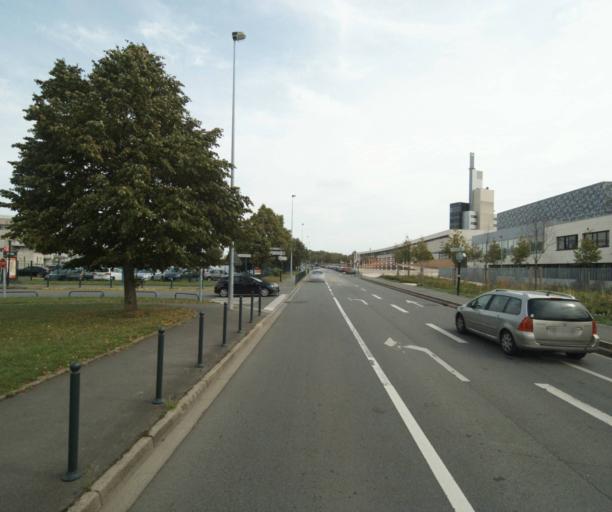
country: FR
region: Nord-Pas-de-Calais
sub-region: Departement du Nord
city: Loos
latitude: 50.6052
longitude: 3.0301
